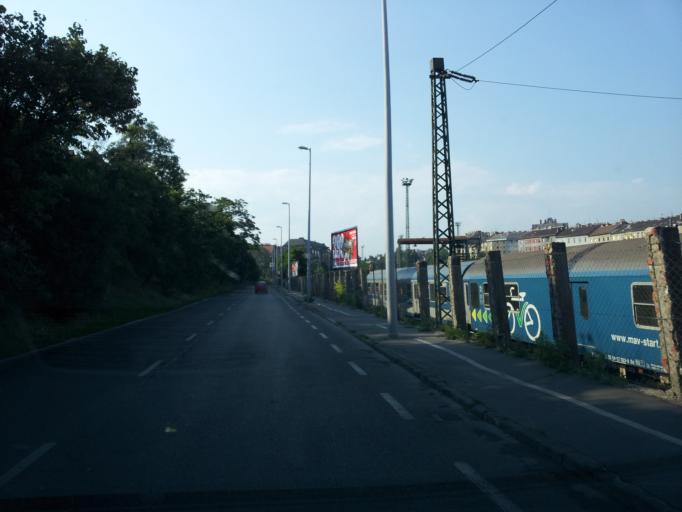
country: HU
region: Budapest
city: Budapest I. keruelet
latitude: 47.4938
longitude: 19.0291
